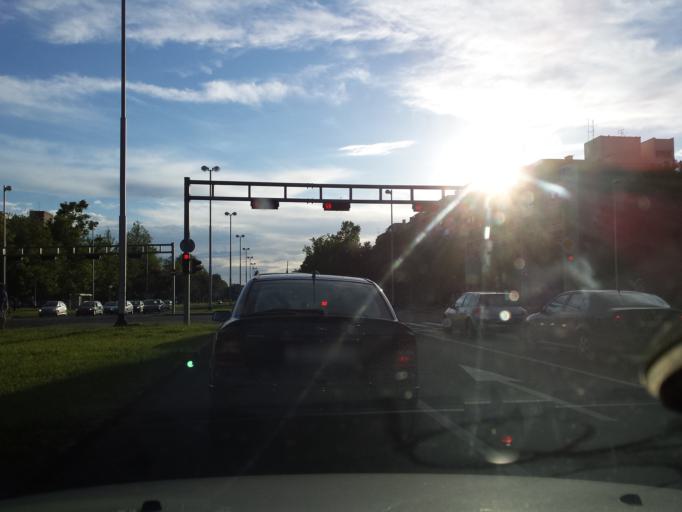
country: HR
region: Grad Zagreb
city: Novi Zagreb
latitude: 45.7682
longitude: 16.0001
